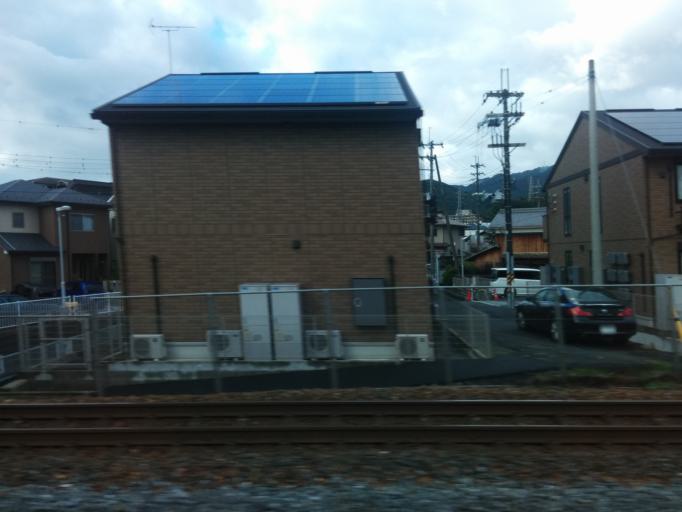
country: JP
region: Shiga Prefecture
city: Otsu-shi
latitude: 34.9846
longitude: 135.8921
